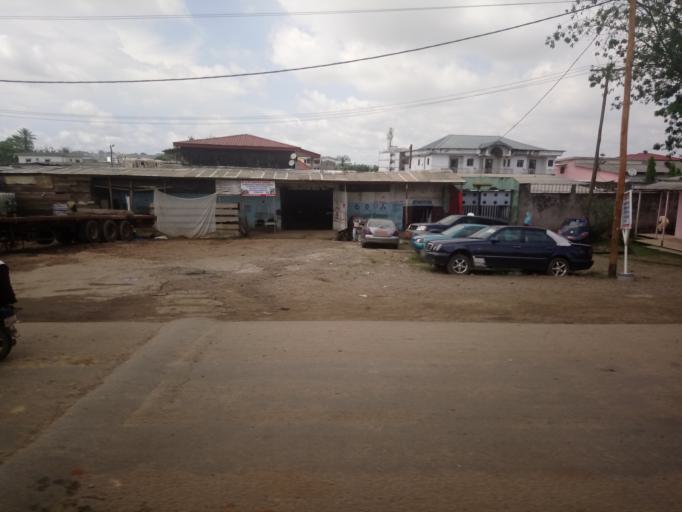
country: CM
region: Littoral
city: Douala
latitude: 4.0224
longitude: 9.7207
